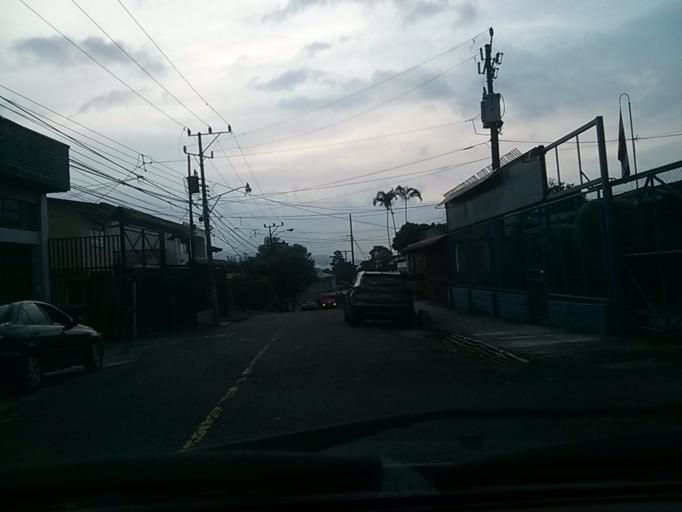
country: CR
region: San Jose
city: San Pedro
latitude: 9.9303
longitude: -84.0408
